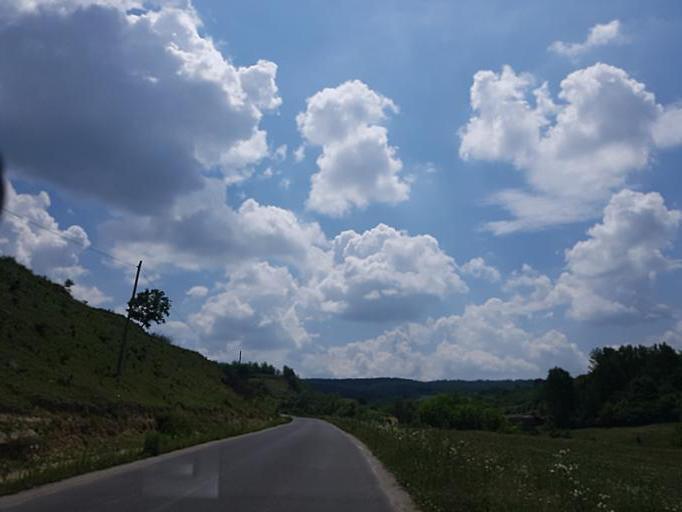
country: RO
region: Sibiu
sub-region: Comuna Seica Mica
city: Seica Mica
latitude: 46.0504
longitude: 24.1458
